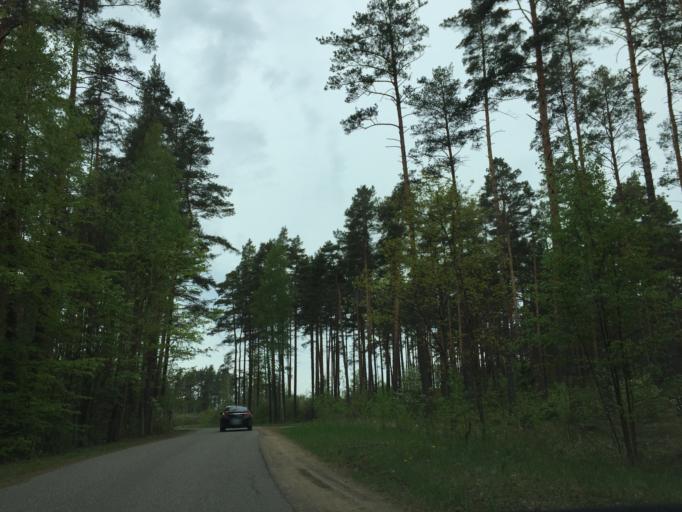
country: LV
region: Adazi
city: Adazi
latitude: 57.0589
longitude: 24.3260
